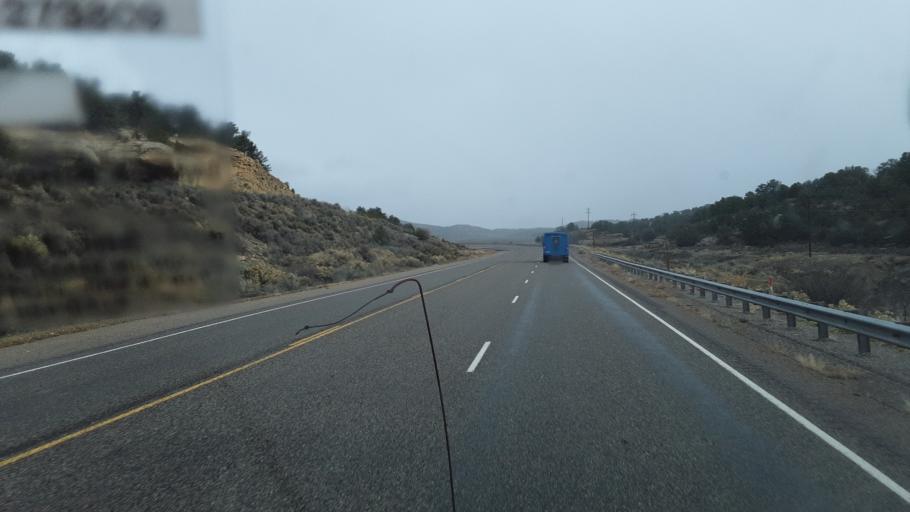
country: US
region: New Mexico
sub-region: Rio Arriba County
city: Tierra Amarilla
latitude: 36.4336
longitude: -106.4758
